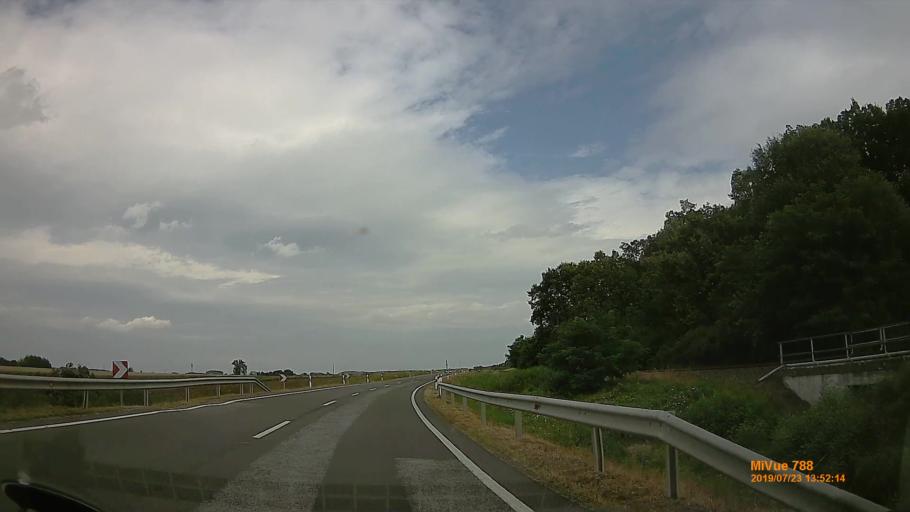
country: HU
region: Hajdu-Bihar
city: Polgar
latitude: 47.8999
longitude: 21.1577
